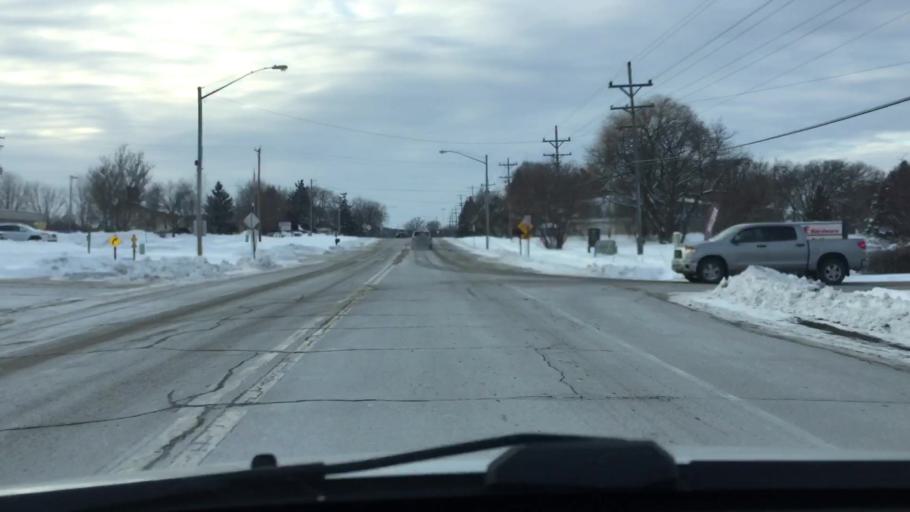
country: US
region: Wisconsin
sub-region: Waukesha County
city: Sussex
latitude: 43.1339
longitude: -88.2303
